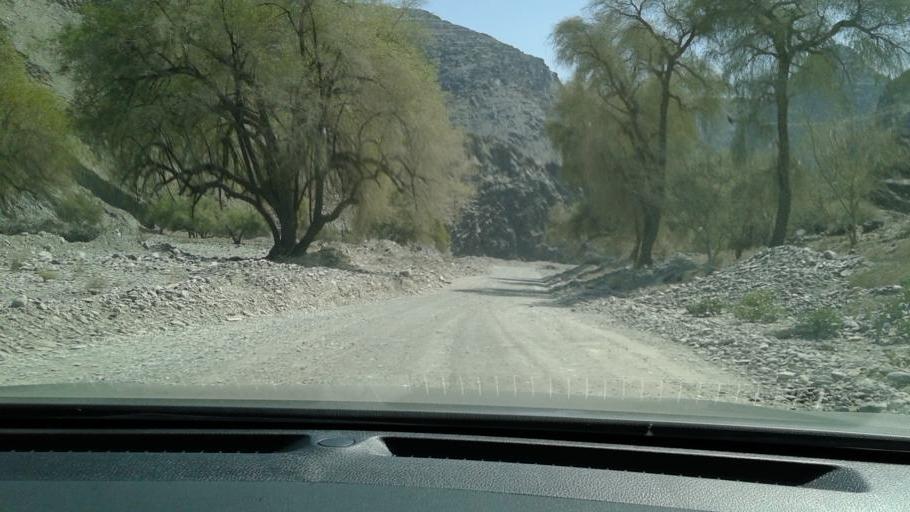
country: OM
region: Al Batinah
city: Bayt al `Awabi
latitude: 23.2607
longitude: 57.4421
